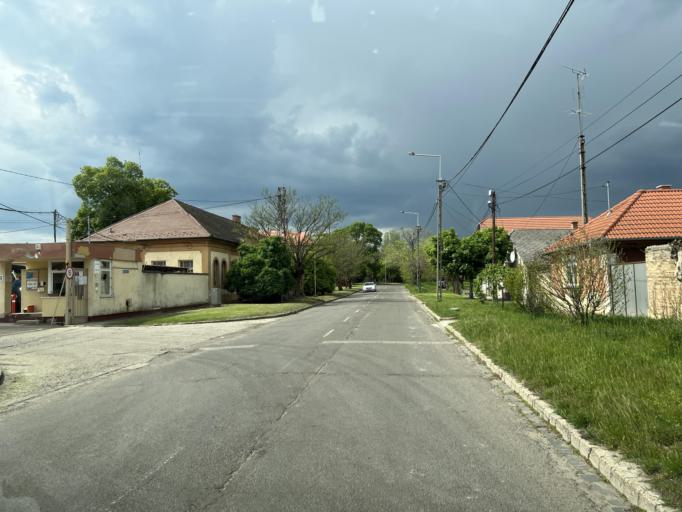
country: HU
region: Pest
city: Nagykoros
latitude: 47.0359
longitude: 19.7619
